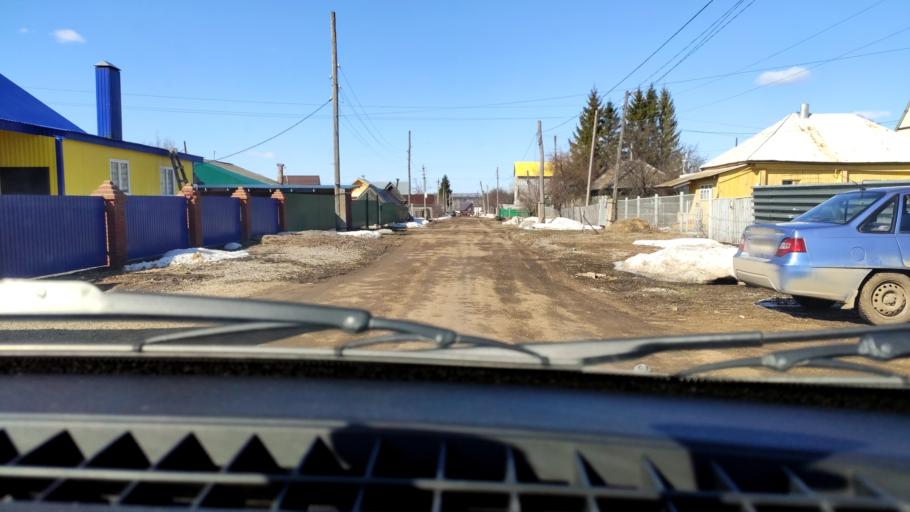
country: RU
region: Bashkortostan
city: Iglino
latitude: 54.8183
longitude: 56.4087
